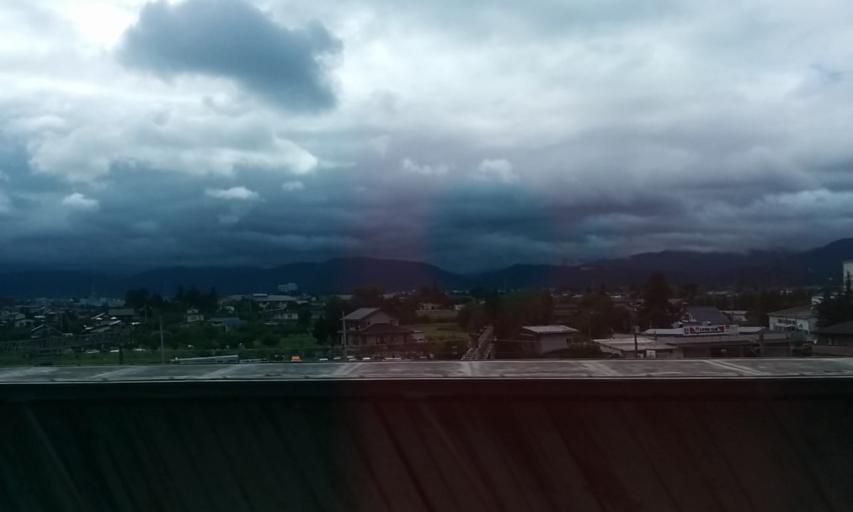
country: JP
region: Fukushima
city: Fukushima-shi
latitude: 37.7990
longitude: 140.4776
